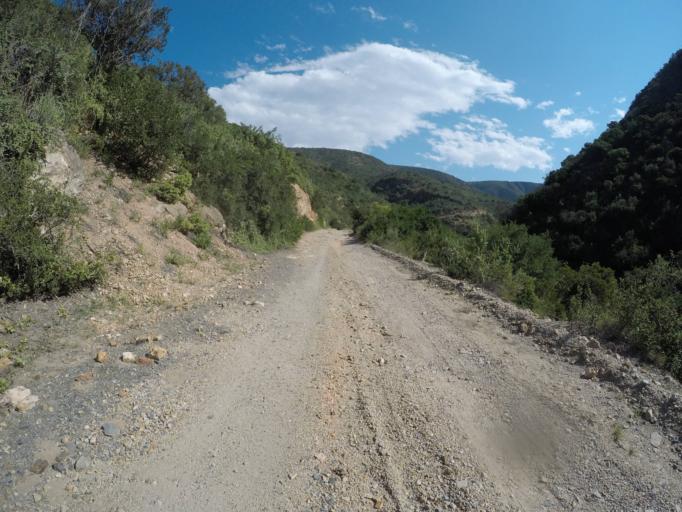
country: ZA
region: Eastern Cape
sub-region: Cacadu District Municipality
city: Kareedouw
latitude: -33.6553
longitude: 24.3614
